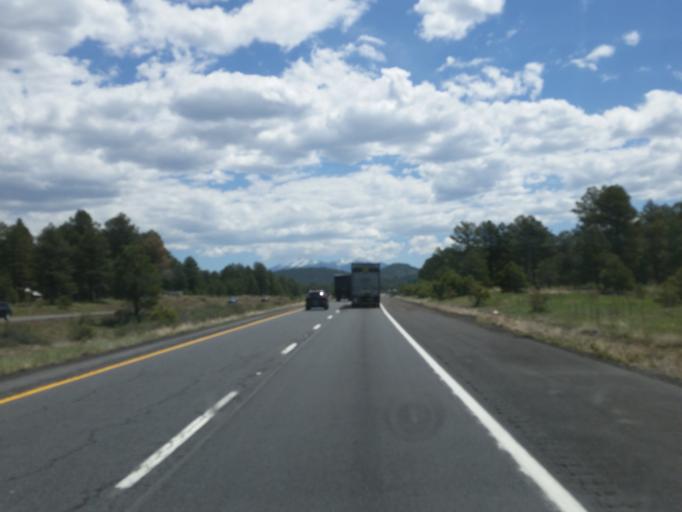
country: US
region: Arizona
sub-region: Coconino County
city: Parks
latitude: 35.2533
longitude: -111.9472
